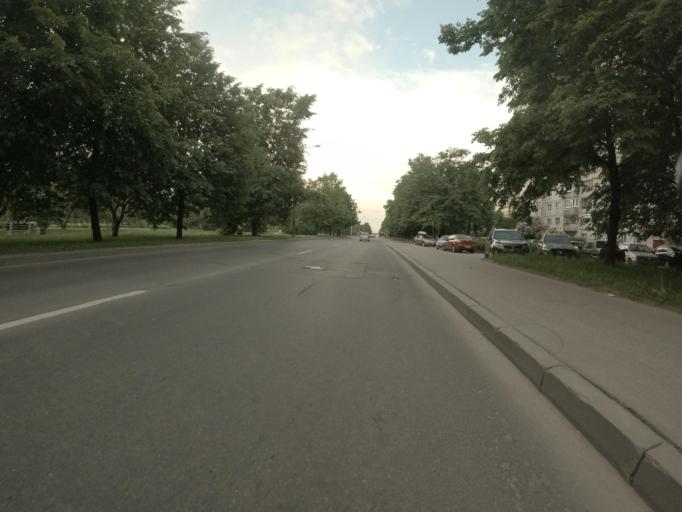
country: RU
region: St.-Petersburg
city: Kupchino
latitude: 59.8364
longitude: 30.3197
